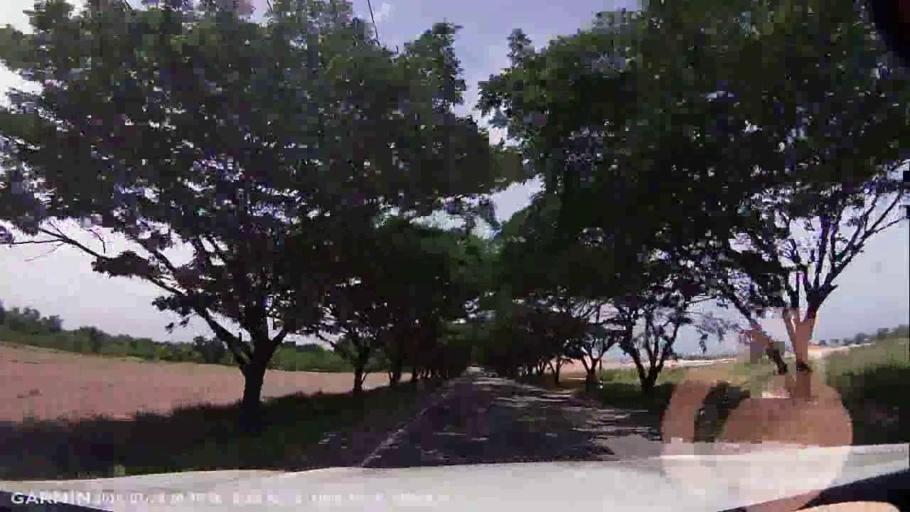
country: TH
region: Chon Buri
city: Phatthaya
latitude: 12.8972
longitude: 100.9857
